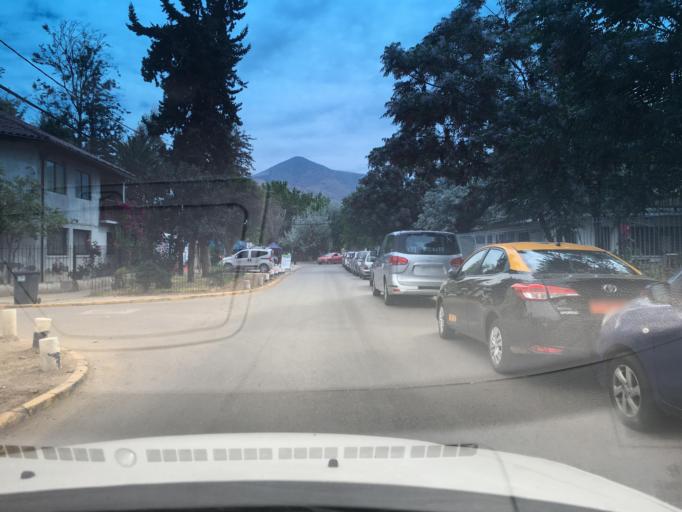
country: CL
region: Santiago Metropolitan
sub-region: Provincia de Santiago
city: Santiago
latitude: -33.3849
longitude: -70.6453
